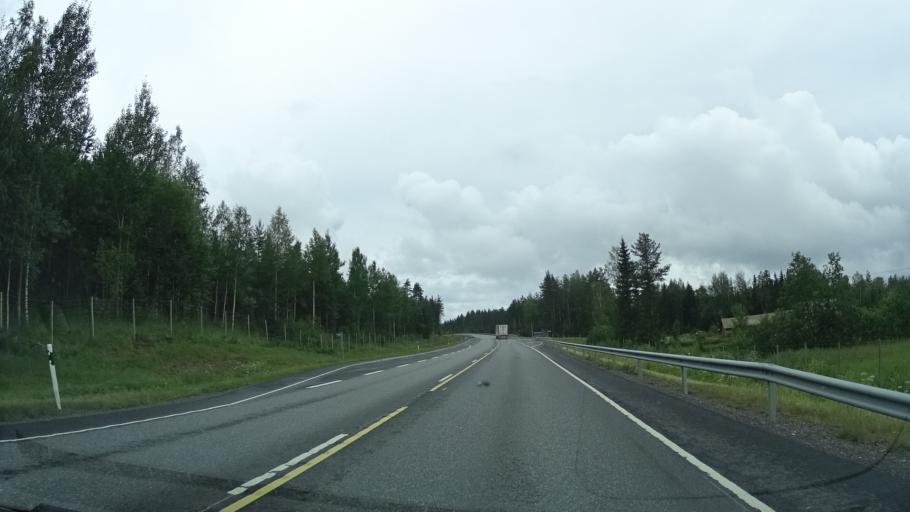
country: FI
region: Uusimaa
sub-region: Helsinki
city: Karkkila
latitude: 60.5839
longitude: 24.1280
